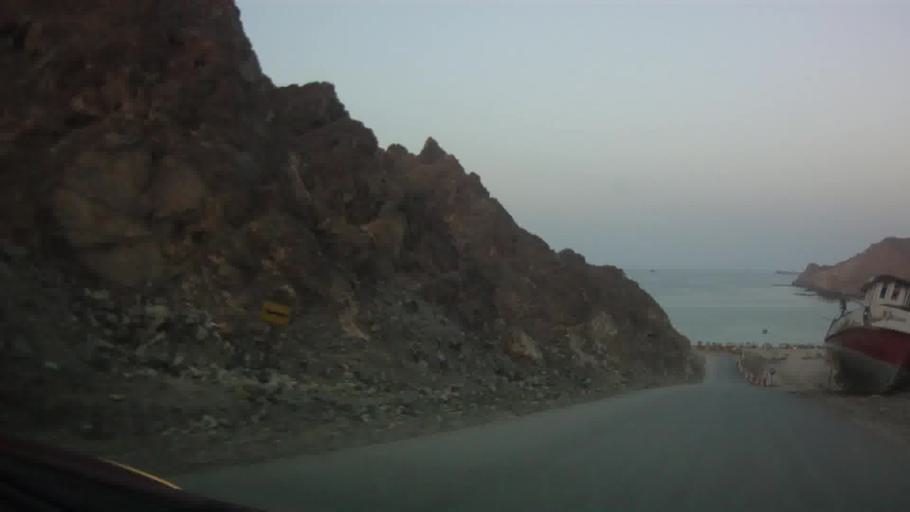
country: OM
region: Muhafazat Masqat
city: Muscat
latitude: 23.6326
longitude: 58.5458
